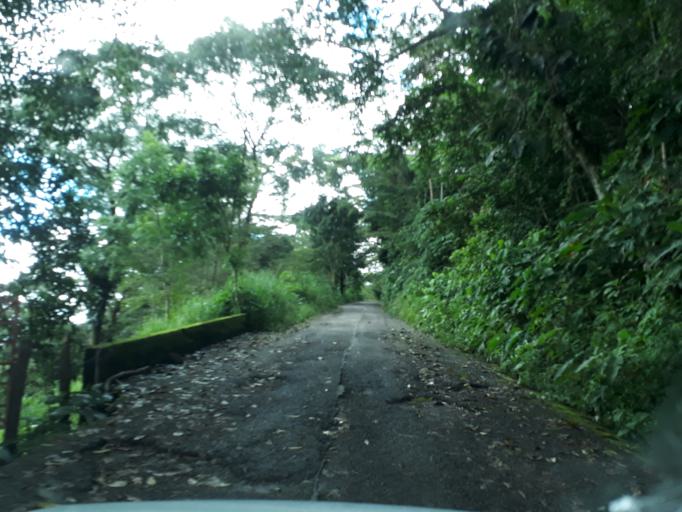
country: CO
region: Cundinamarca
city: Medina
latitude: 4.5636
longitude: -73.3637
